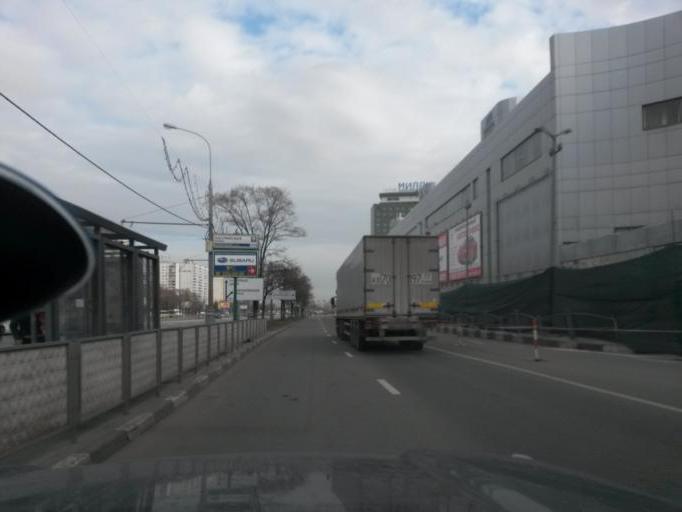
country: RU
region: Moscow
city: Orekhovo-Borisovo
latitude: 55.6157
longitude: 37.7155
